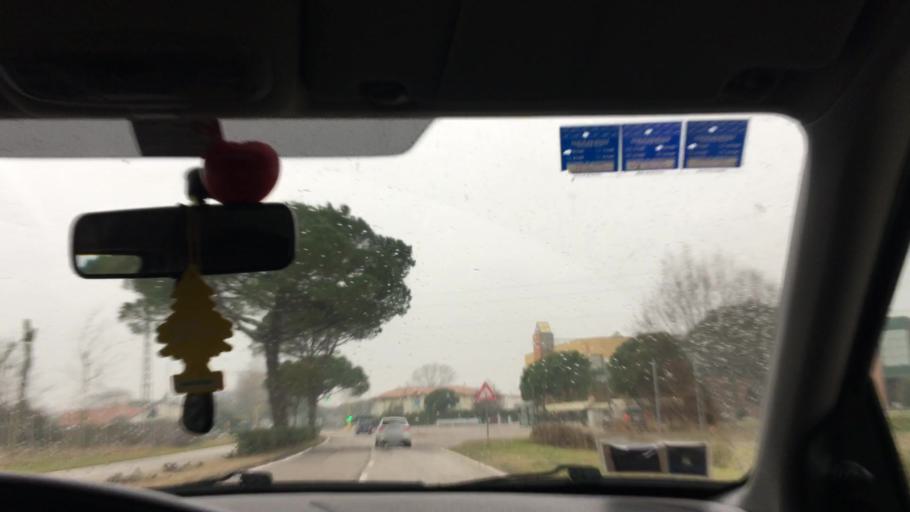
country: IT
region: Veneto
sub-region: Provincia di Venezia
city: Lido di Iesolo
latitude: 45.5120
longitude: 12.6493
